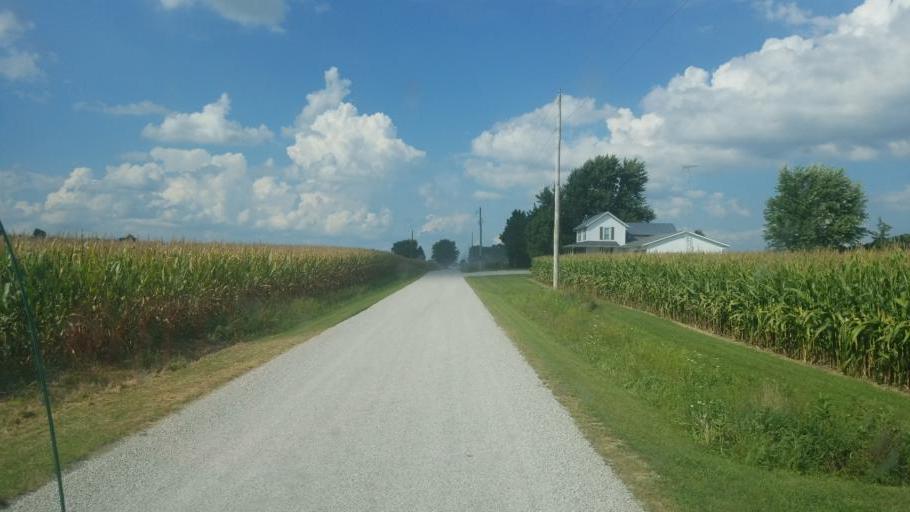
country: US
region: Ohio
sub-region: Huron County
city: Willard
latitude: 40.9892
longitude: -82.7966
